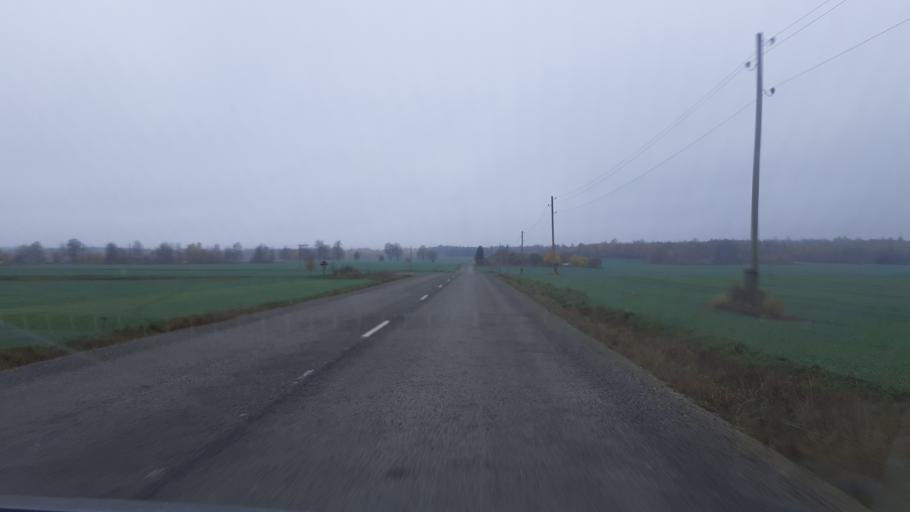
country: LV
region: Kuldigas Rajons
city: Kuldiga
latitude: 56.9632
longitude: 21.9069
